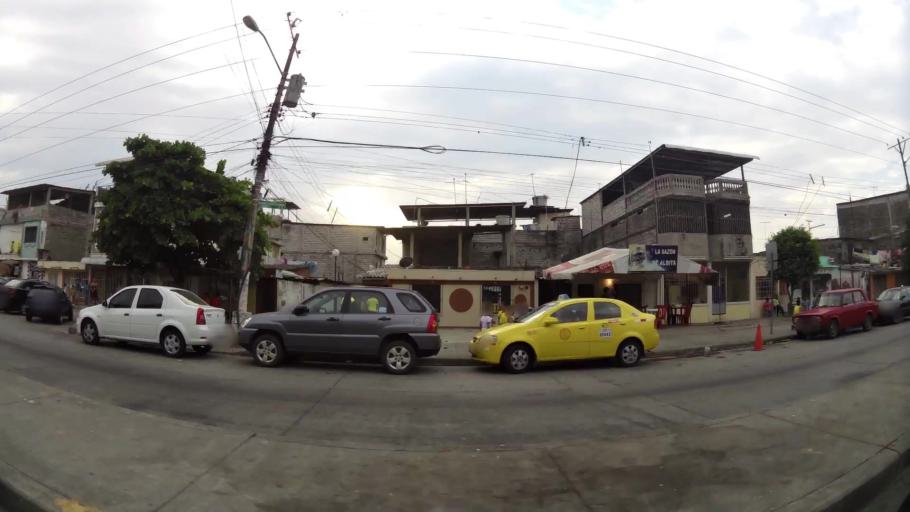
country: EC
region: Guayas
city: Guayaquil
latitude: -2.2559
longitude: -79.8839
